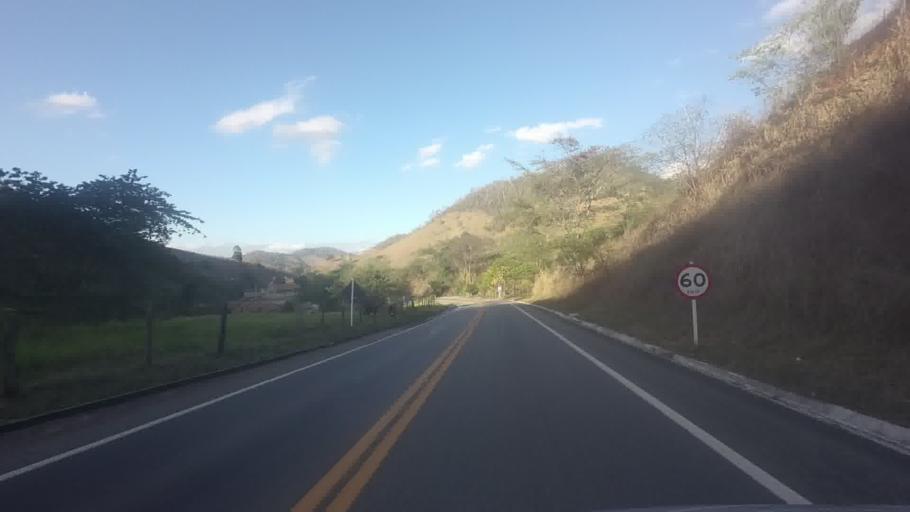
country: BR
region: Espirito Santo
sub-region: Cachoeiro De Itapemirim
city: Cachoeiro de Itapemirim
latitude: -20.8396
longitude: -41.2320
